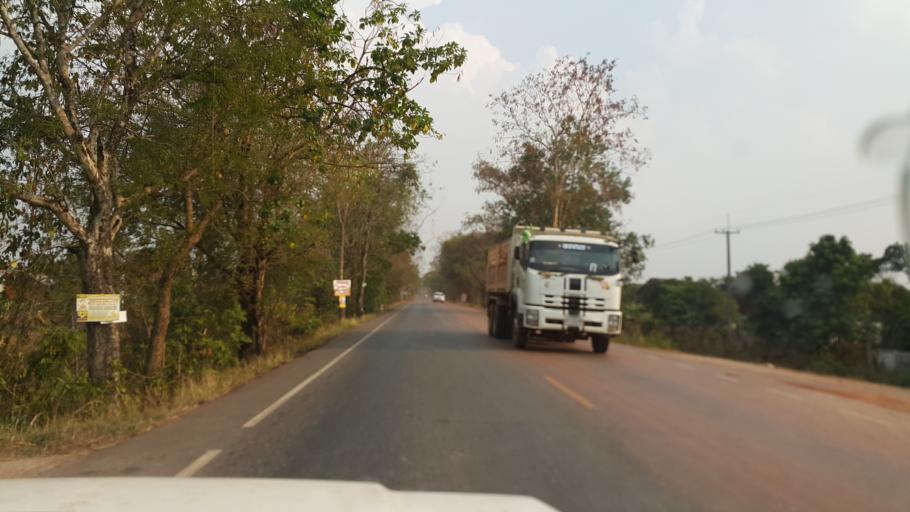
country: TH
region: Nakhon Phanom
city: Ban Phaeng
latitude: 17.8701
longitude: 104.2523
